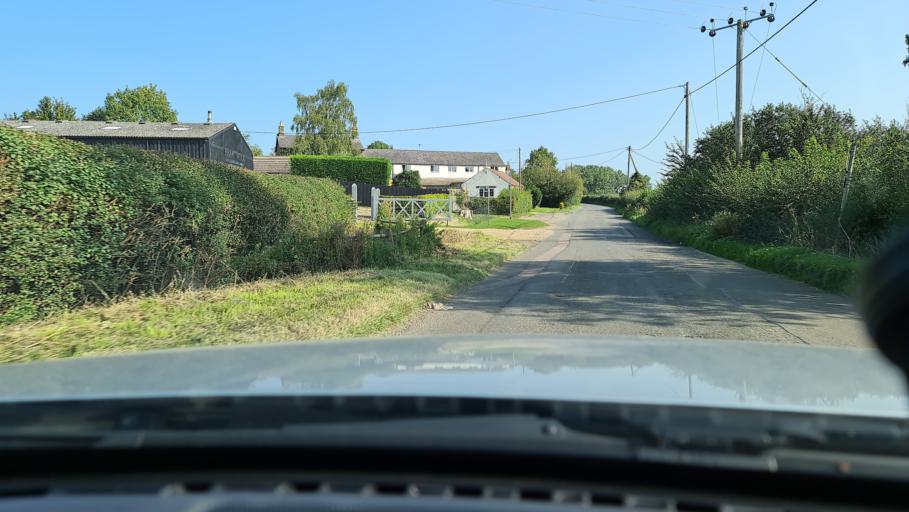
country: GB
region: England
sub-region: Northamptonshire
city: Brackley
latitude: 52.1322
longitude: -1.1749
